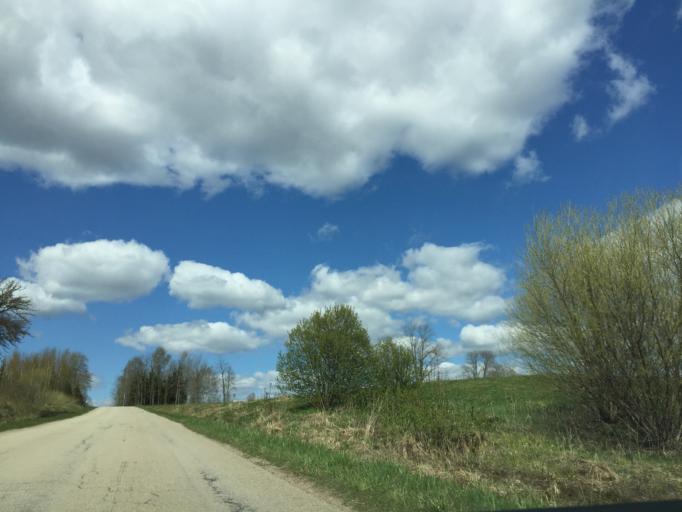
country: LV
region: Rezekne
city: Rezekne
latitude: 56.5572
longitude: 27.1468
